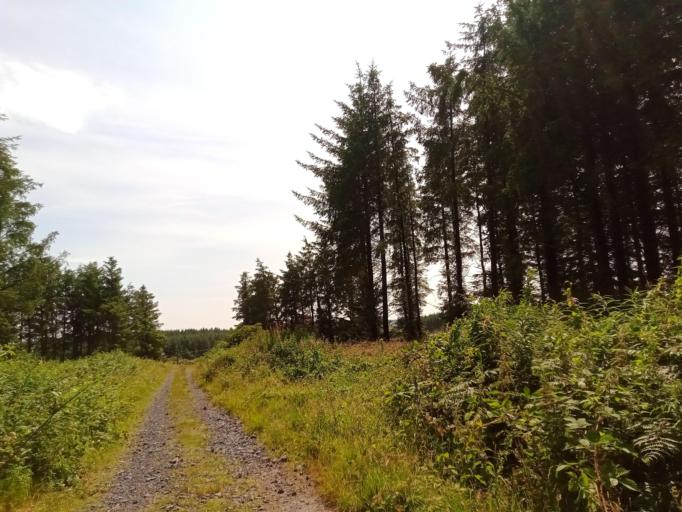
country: IE
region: Leinster
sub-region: Kilkenny
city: Ballyragget
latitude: 52.8021
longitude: -7.4543
